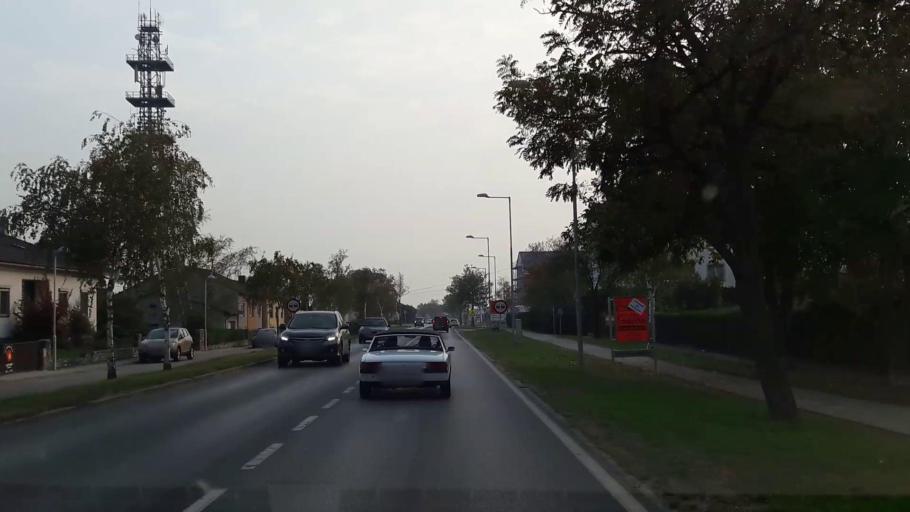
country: AT
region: Burgenland
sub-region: Politischer Bezirk Neusiedl am See
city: Neusiedl am See
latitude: 47.9637
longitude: 16.8371
